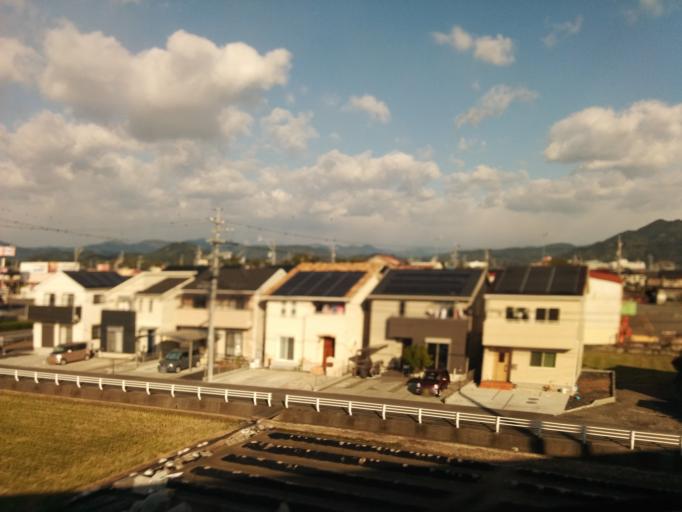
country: JP
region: Shizuoka
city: Yaizu
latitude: 34.8675
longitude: 138.3005
